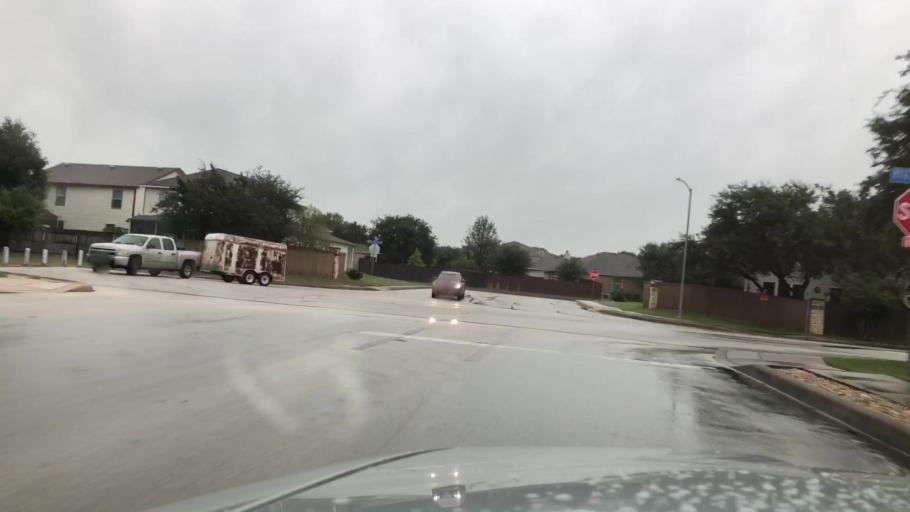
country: US
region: Texas
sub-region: Bexar County
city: Helotes
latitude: 29.5516
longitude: -98.6466
